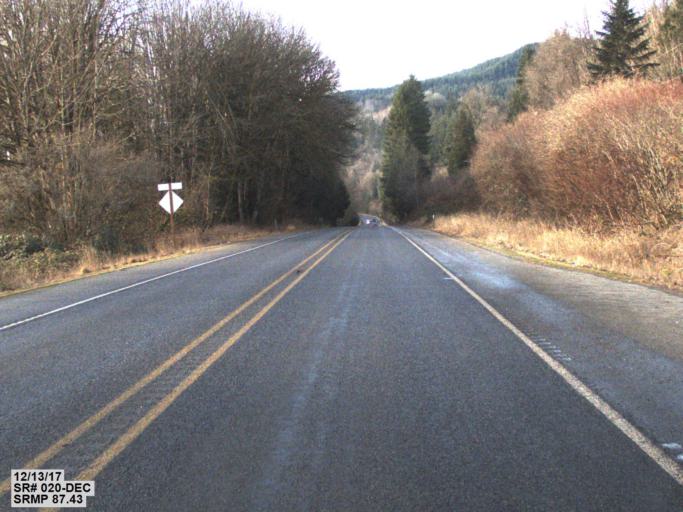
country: US
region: Washington
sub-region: Snohomish County
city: Darrington
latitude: 48.5403
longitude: -121.7822
